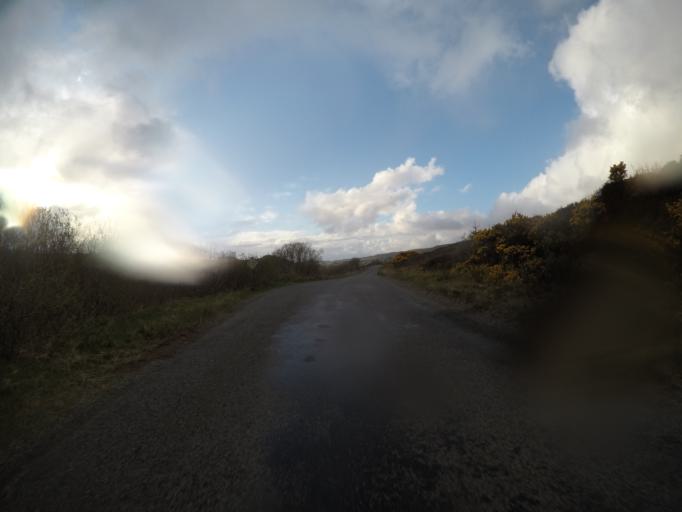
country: GB
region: Scotland
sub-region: Highland
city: Isle of Skye
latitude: 57.4691
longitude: -6.2993
